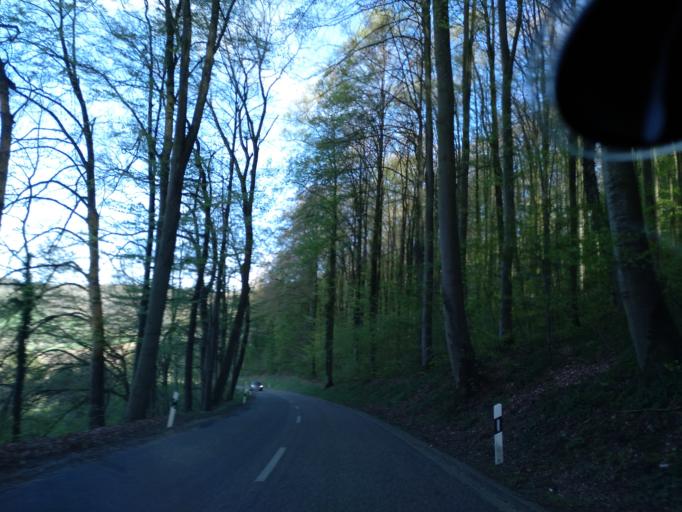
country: DE
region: Baden-Wuerttemberg
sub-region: Regierungsbezirk Stuttgart
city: Langenburg
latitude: 49.2204
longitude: 9.8960
